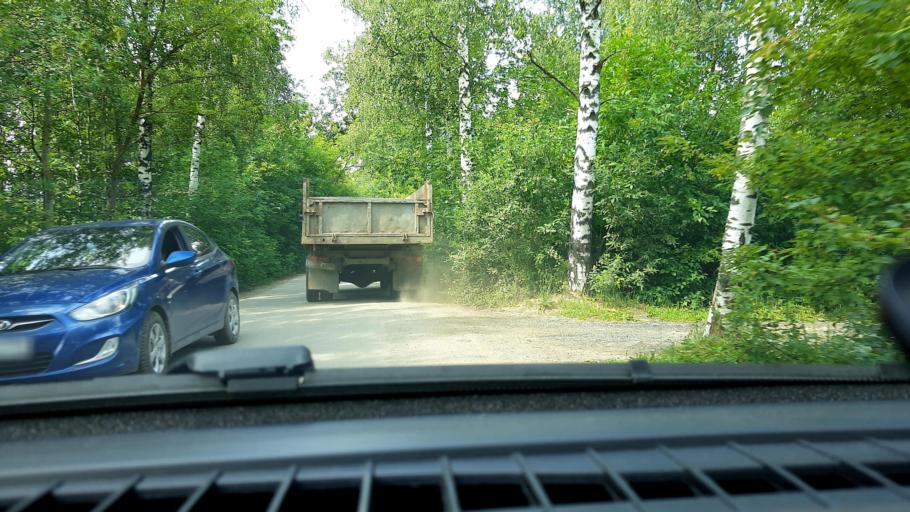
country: RU
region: Nizjnij Novgorod
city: Gorbatovka
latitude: 56.2492
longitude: 43.8171
